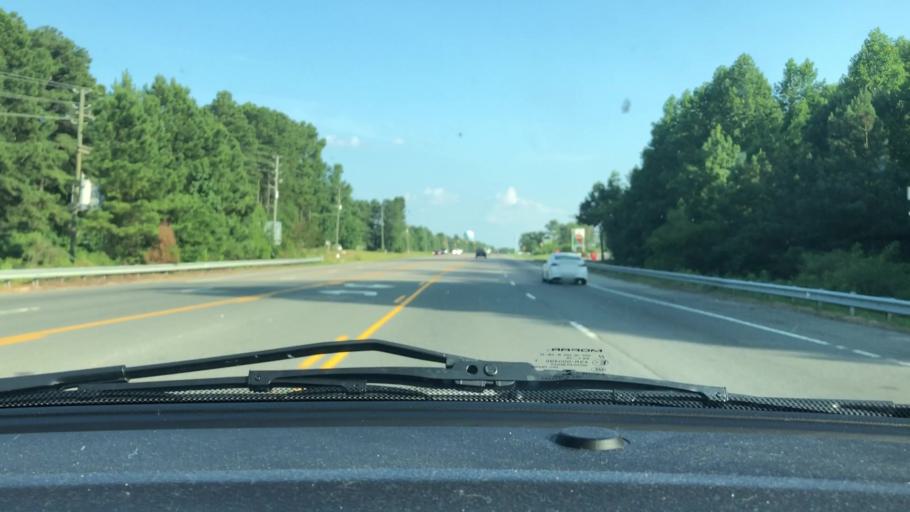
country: US
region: North Carolina
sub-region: Lee County
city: Broadway
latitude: 35.4258
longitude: -79.1210
